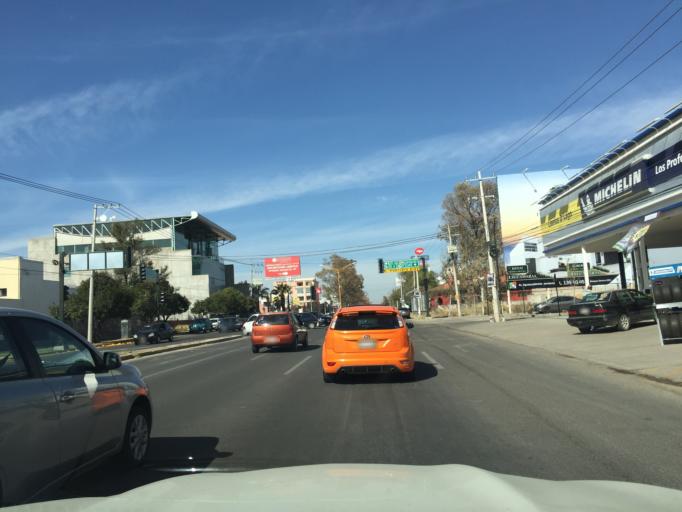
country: MX
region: Aguascalientes
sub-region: Jesus Maria
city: El Llano
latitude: 21.9195
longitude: -102.2976
